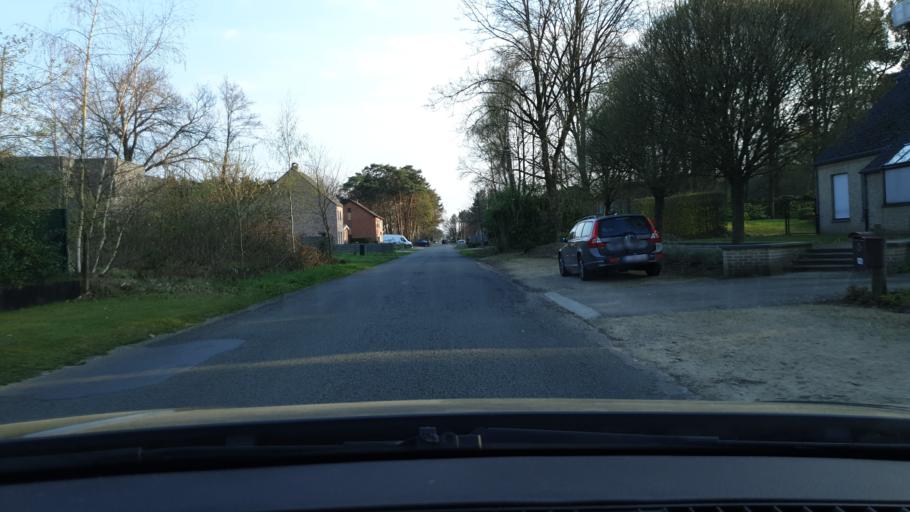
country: BE
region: Flanders
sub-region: Provincie Antwerpen
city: Geel
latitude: 51.1343
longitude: 5.0073
